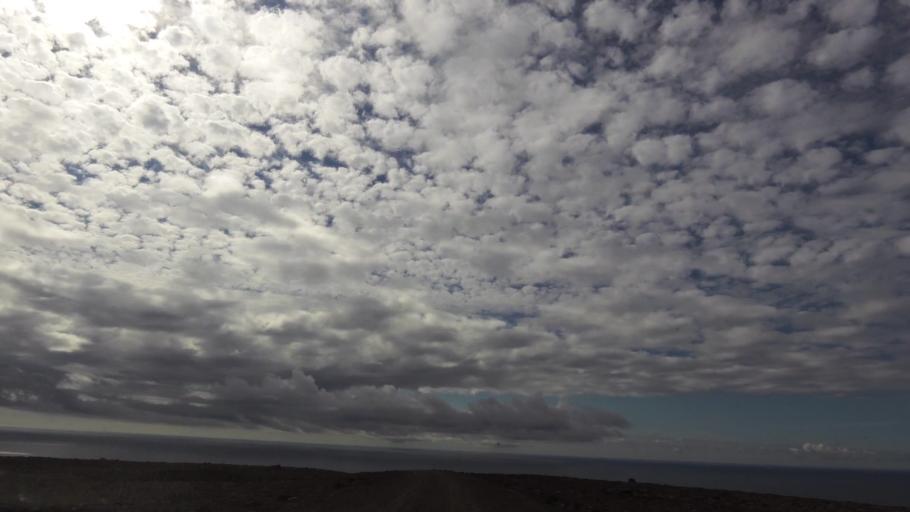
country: IS
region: West
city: Olafsvik
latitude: 65.6208
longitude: -24.3110
